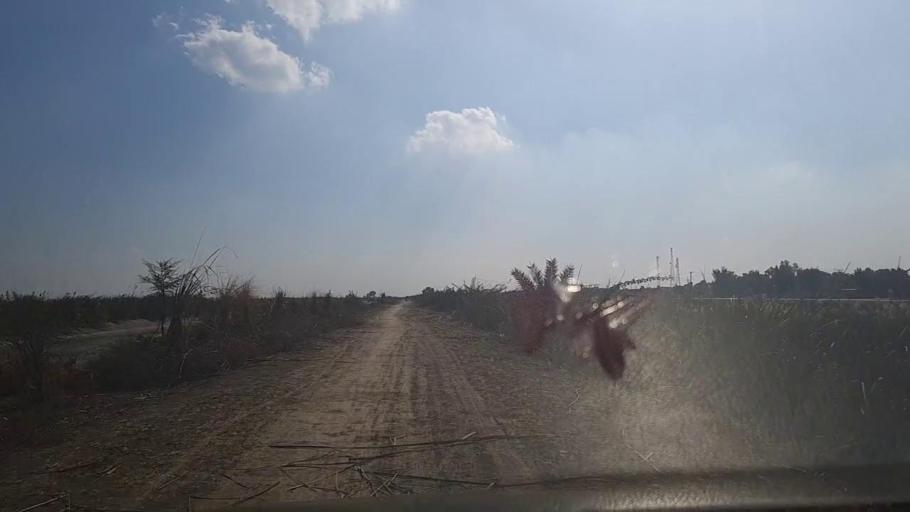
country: PK
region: Sindh
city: Tando Mittha Khan
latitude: 25.8036
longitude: 69.0732
